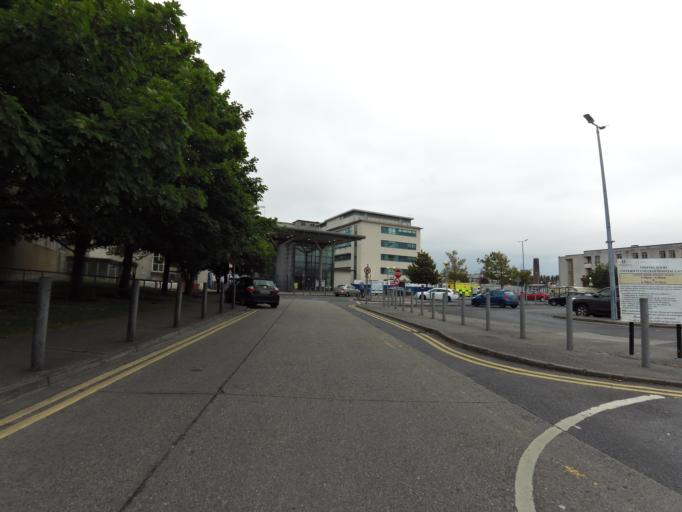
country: IE
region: Connaught
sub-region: County Galway
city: Gaillimh
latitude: 53.2764
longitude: -9.0646
